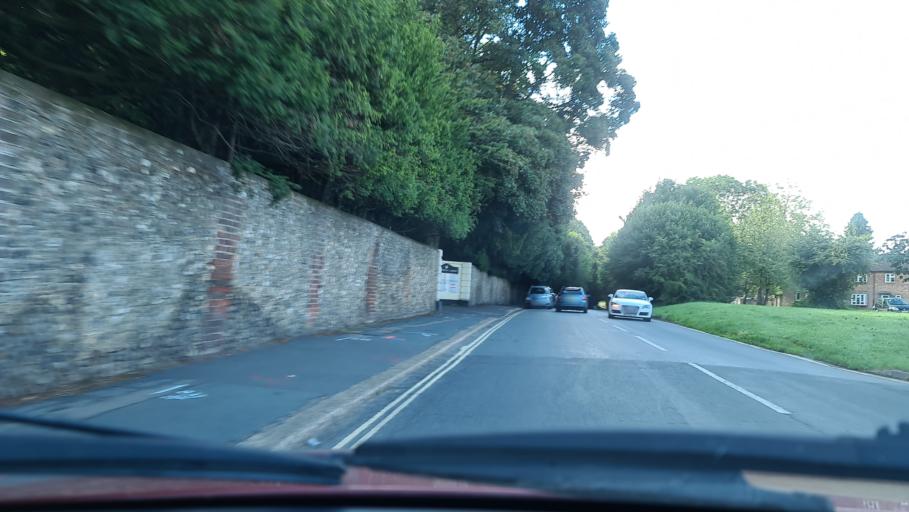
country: GB
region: England
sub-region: Buckinghamshire
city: Great Missenden
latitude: 51.7007
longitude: -0.7044
